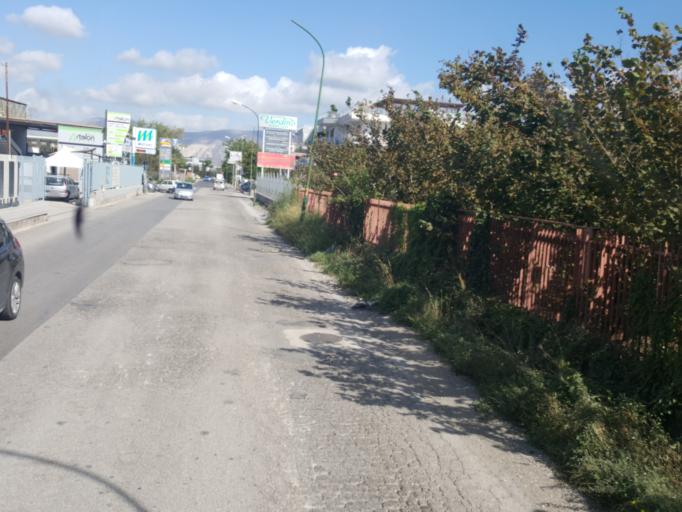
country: IT
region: Campania
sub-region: Provincia di Napoli
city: Nola
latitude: 40.9124
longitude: 14.5272
